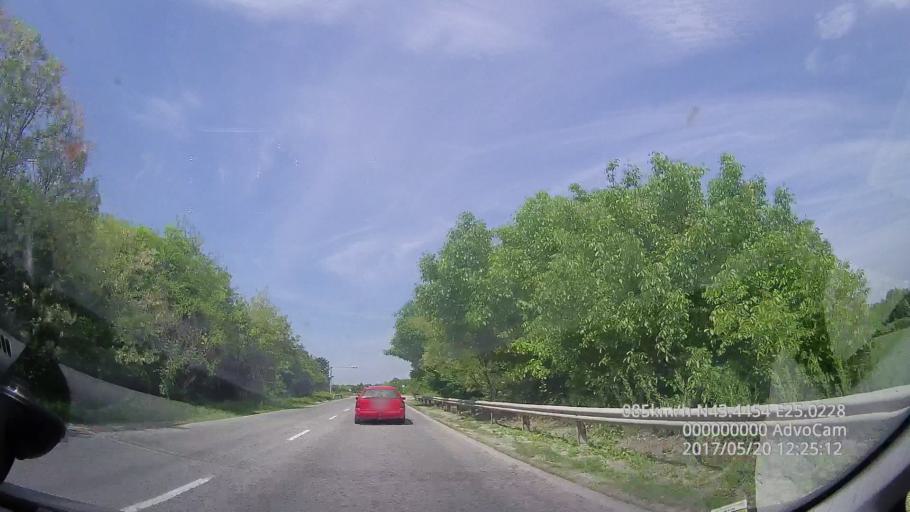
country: BG
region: Pleven
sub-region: Obshtina Levski
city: Levski
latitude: 43.4454
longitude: 25.0224
